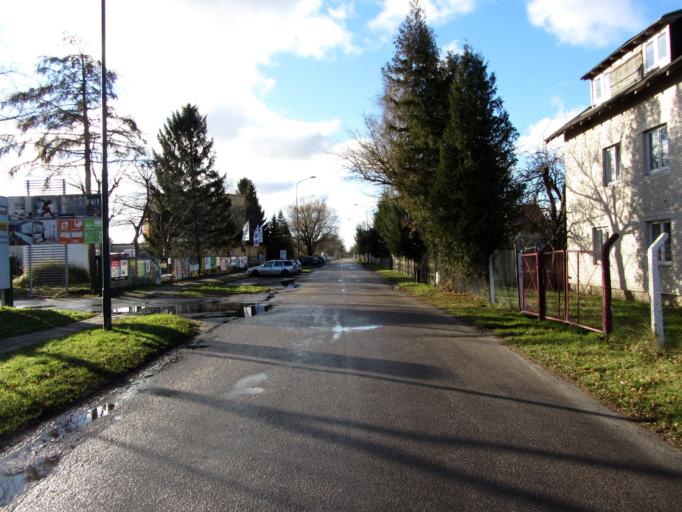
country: PL
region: West Pomeranian Voivodeship
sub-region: Powiat kolobrzeski
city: Kolobrzeg
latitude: 54.1737
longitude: 15.5484
